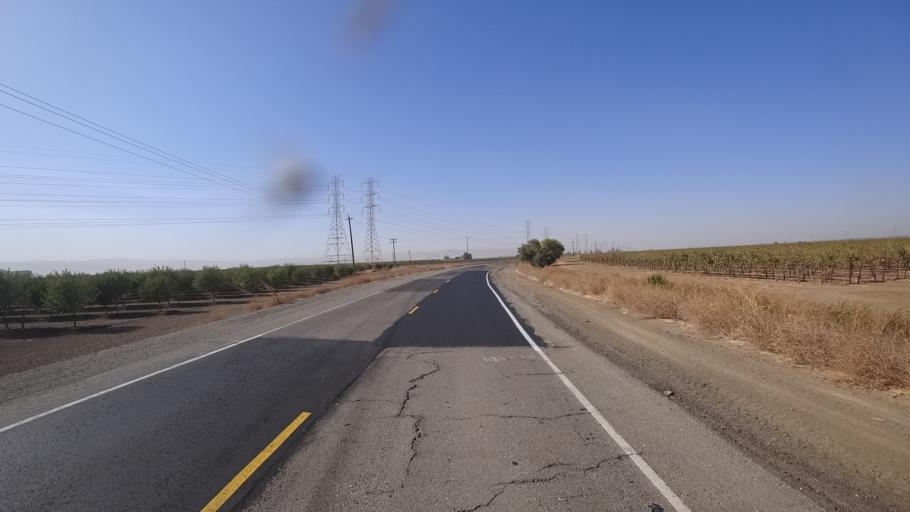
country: US
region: California
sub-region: Yolo County
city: Esparto
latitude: 38.7233
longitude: -121.9690
